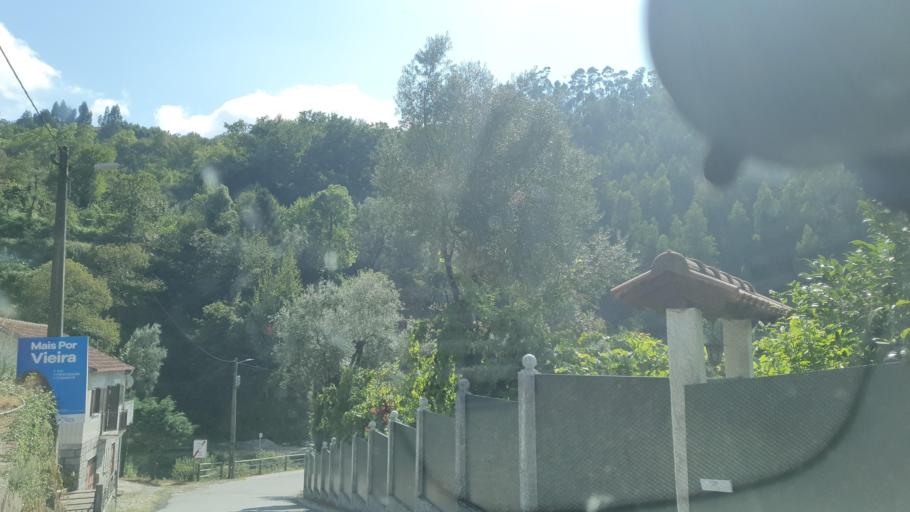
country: PT
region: Braga
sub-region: Vieira do Minho
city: Real
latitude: 41.6689
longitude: -8.1674
